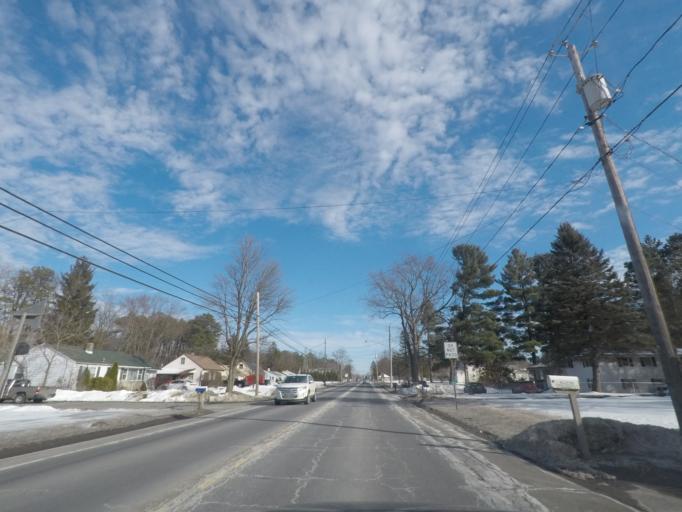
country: US
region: New York
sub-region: Schenectady County
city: Rotterdam
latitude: 42.7877
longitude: -74.0060
